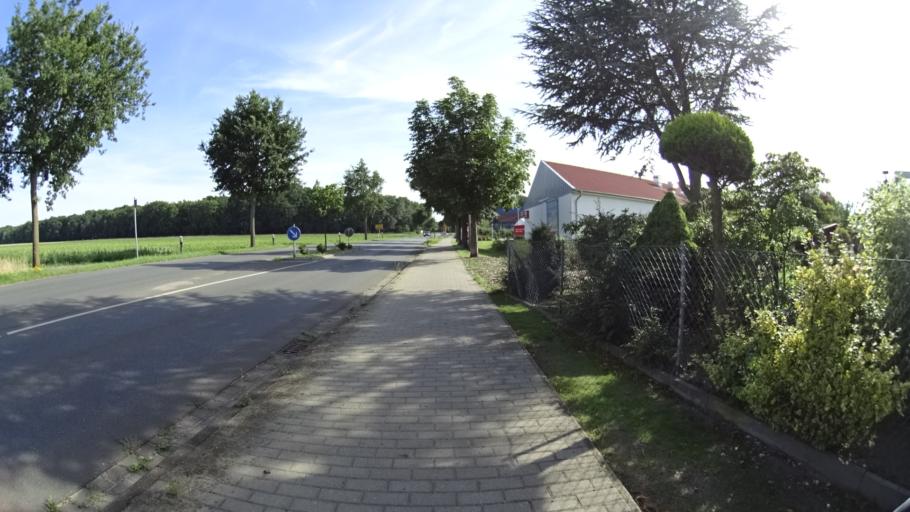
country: DE
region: Lower Saxony
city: Bardowick
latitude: 53.2870
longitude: 10.3961
